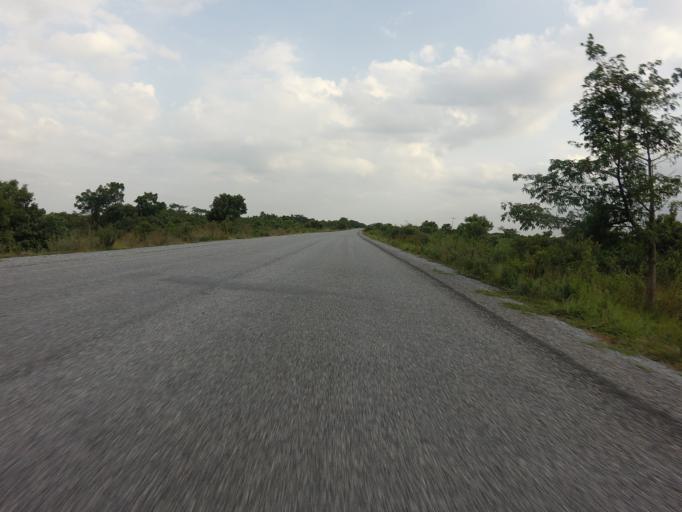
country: GH
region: Volta
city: Ho
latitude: 6.3762
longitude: 0.5330
